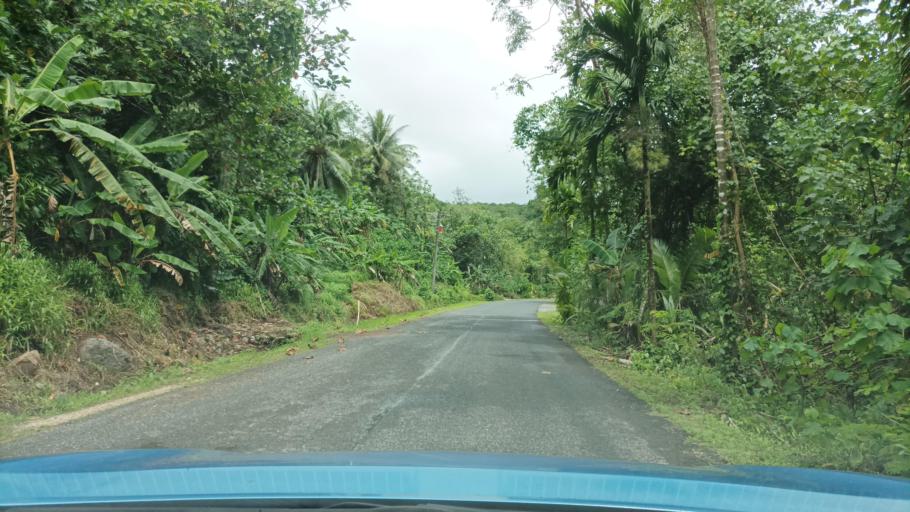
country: FM
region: Pohnpei
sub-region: Madolenihm Municipality
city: Madolenihm Municipality Government
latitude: 6.9135
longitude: 158.3215
